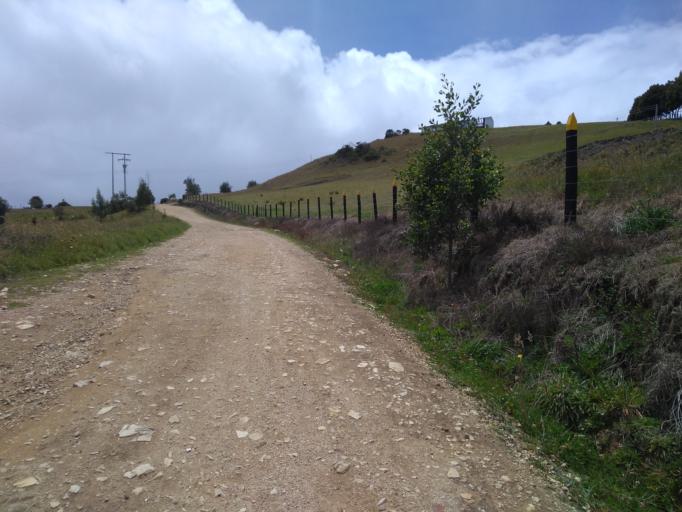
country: CO
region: Boyaca
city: Toca
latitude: 5.5770
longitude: -73.1494
